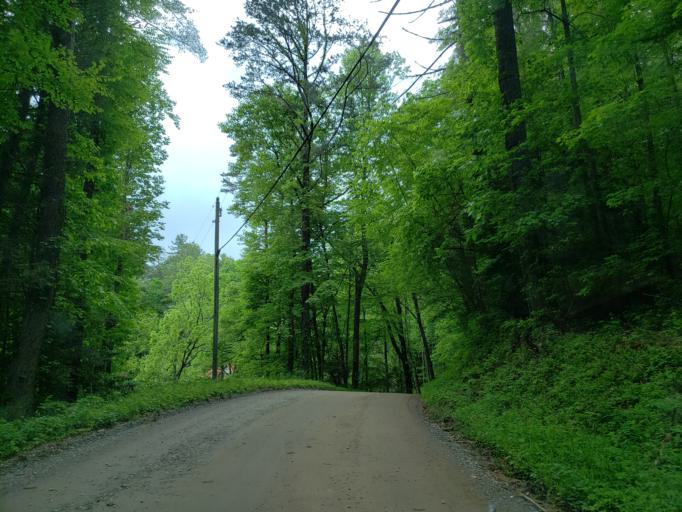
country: US
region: Georgia
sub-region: Fannin County
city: Blue Ridge
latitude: 34.8535
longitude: -84.4194
